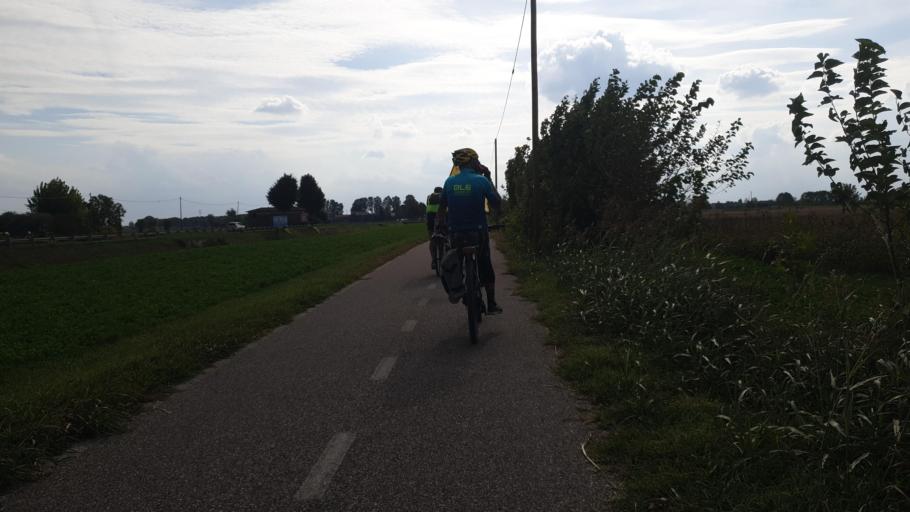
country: IT
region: Veneto
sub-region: Provincia di Vicenza
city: Agugliaro
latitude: 45.3248
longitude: 11.5652
